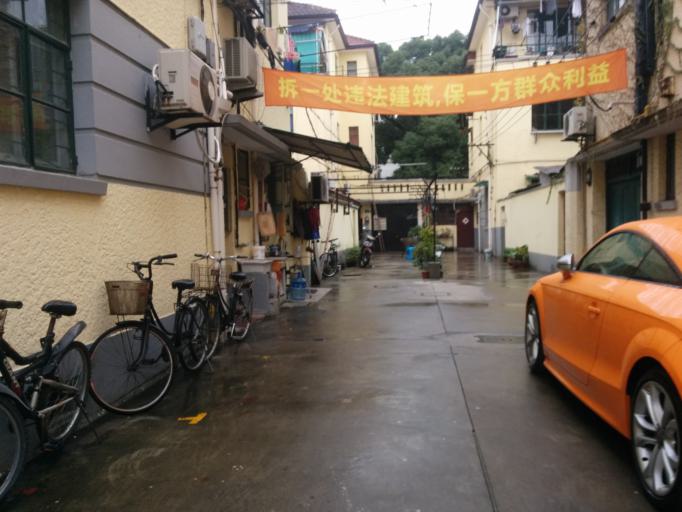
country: CN
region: Shanghai Shi
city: Shanghai
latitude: 31.2264
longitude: 121.4468
